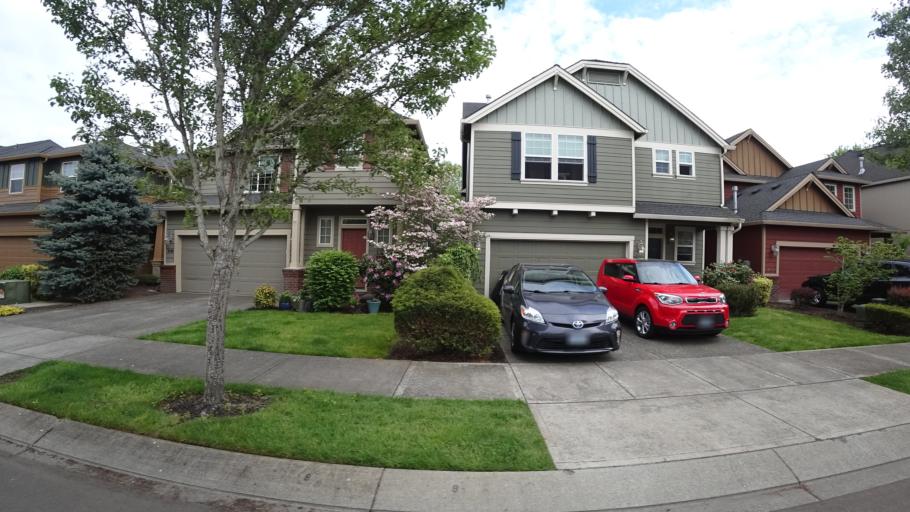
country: US
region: Oregon
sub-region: Washington County
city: Hillsboro
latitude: 45.4934
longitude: -122.9654
